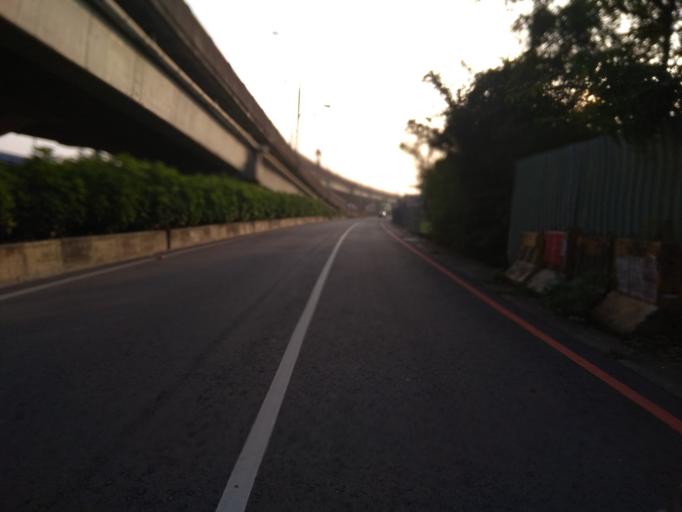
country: TW
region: Taiwan
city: Daxi
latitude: 24.9283
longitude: 121.2107
